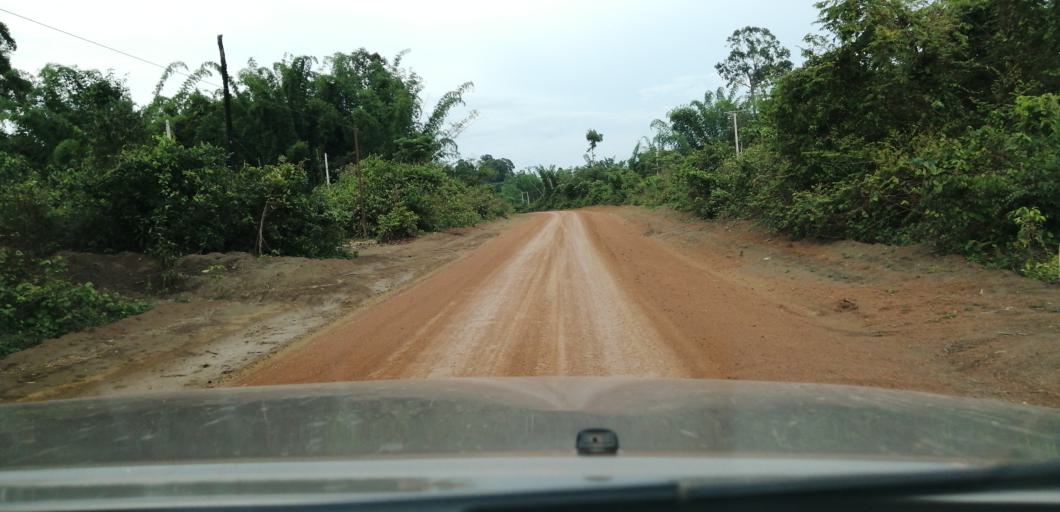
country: LA
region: Champasak
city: Champasak
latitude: 14.6980
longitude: 106.2854
